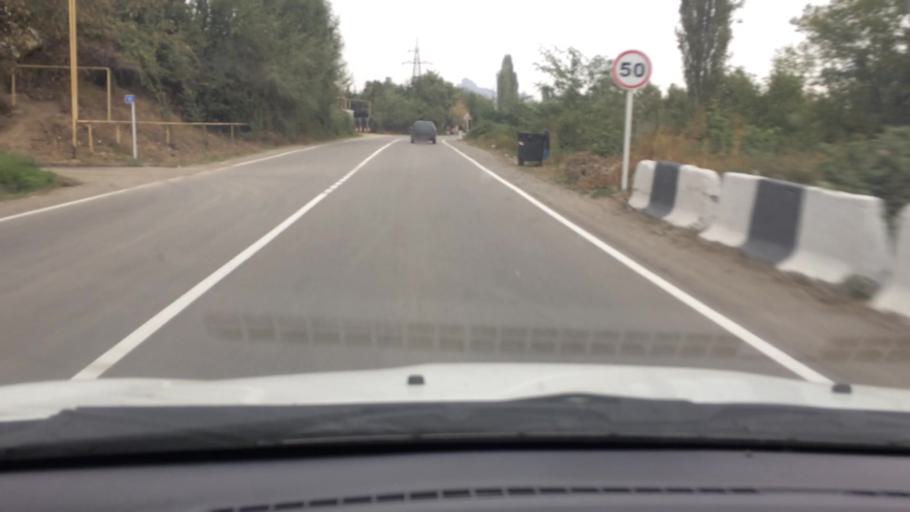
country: GE
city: Naghvarevi
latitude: 41.3245
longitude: 44.7999
